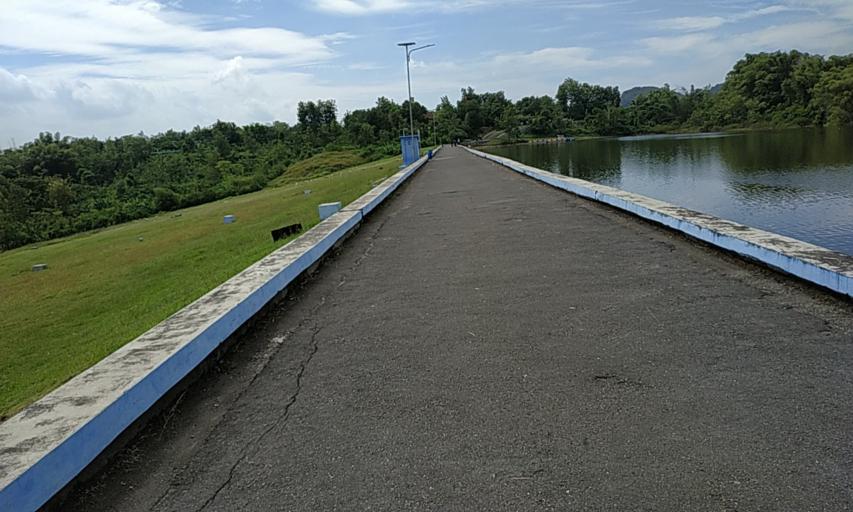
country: ID
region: Central Java
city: Selogiri
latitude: -7.8007
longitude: 110.8991
